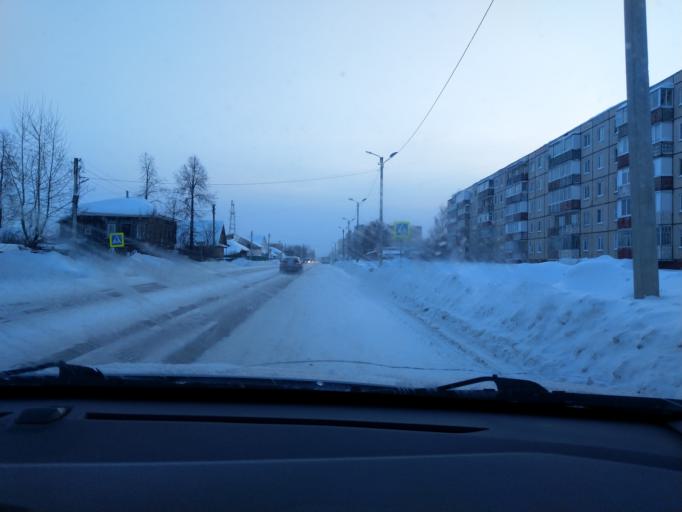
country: RU
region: Perm
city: Dobryanka
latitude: 58.4711
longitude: 56.4066
